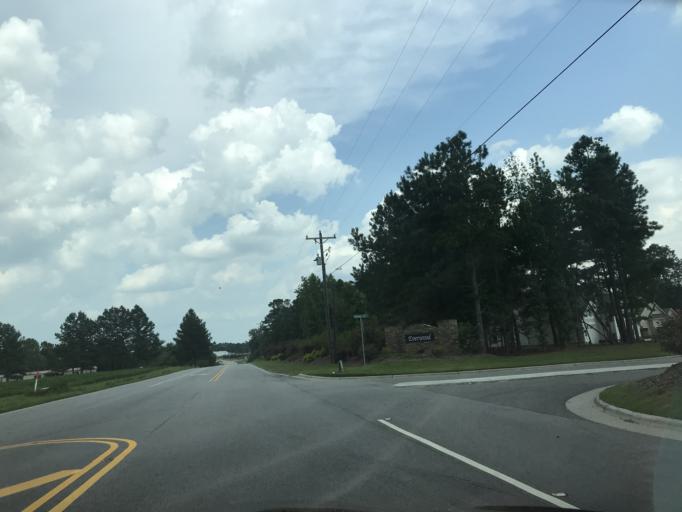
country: US
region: North Carolina
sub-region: Johnston County
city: Four Oaks
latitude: 35.5105
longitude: -78.5252
